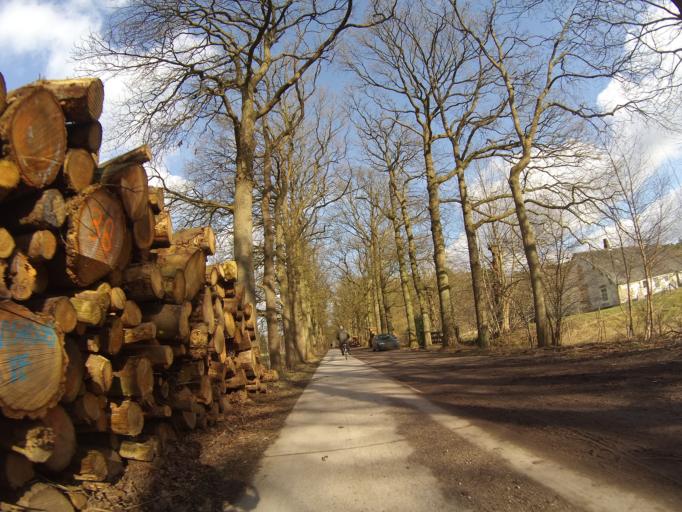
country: NL
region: Utrecht
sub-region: Gemeente Soest
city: Soest
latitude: 52.1640
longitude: 5.2595
